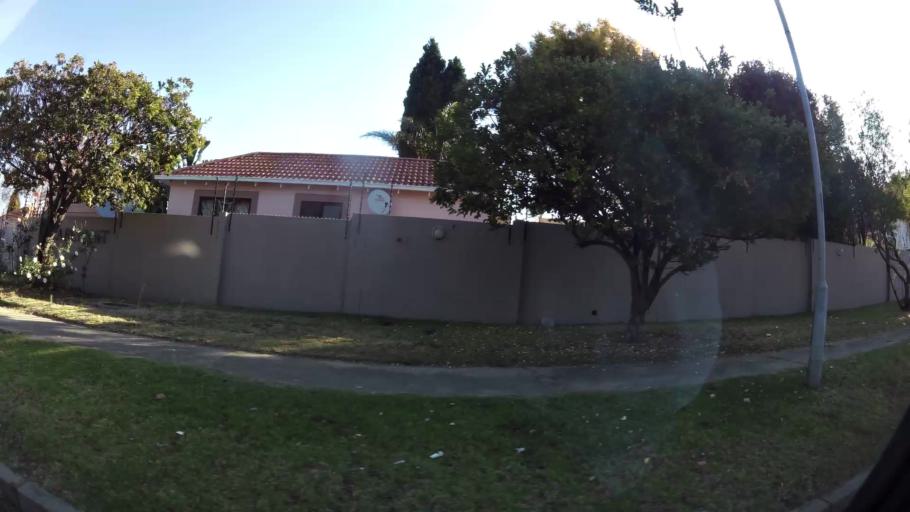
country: ZA
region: Gauteng
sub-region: City of Johannesburg Metropolitan Municipality
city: Roodepoort
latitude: -26.0849
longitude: 27.9636
